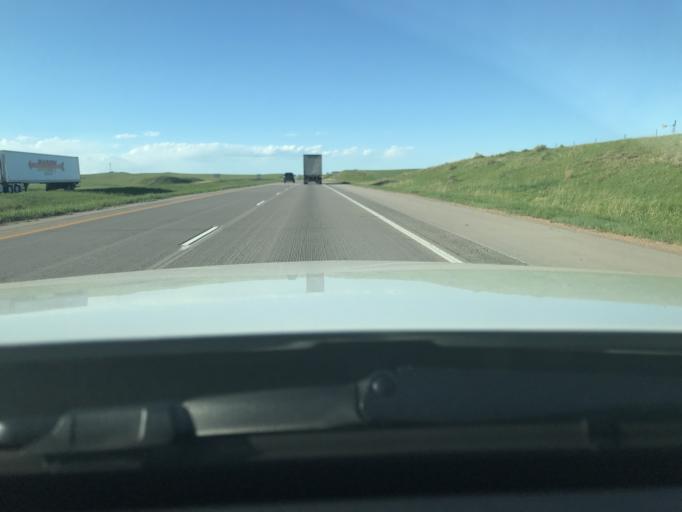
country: US
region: Colorado
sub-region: Larimer County
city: Wellington
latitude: 40.8548
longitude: -104.9616
